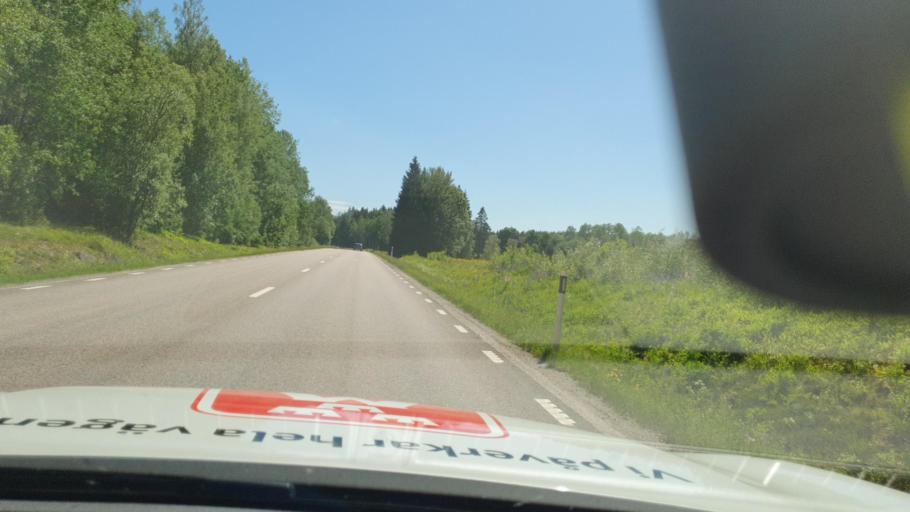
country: SE
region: Vaermland
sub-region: Storfors Kommun
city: Storfors
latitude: 59.5817
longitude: 14.2581
